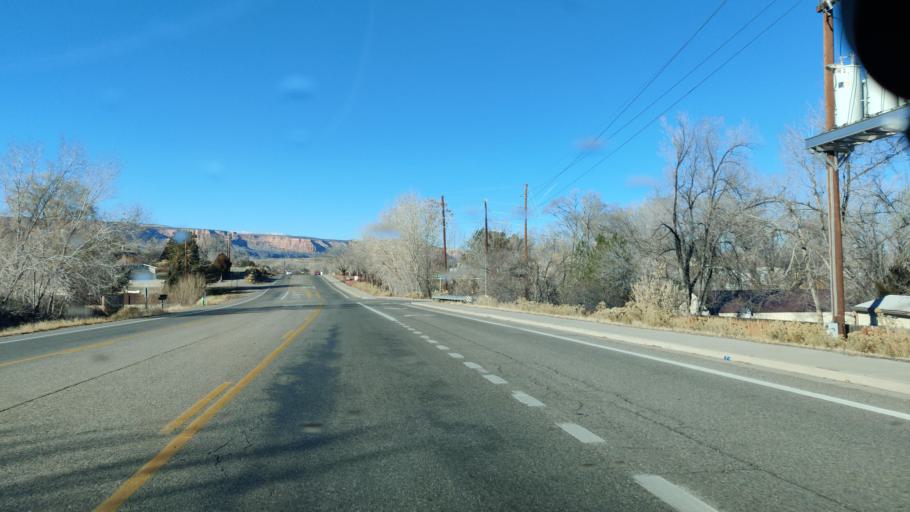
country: US
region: Colorado
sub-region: Mesa County
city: Redlands
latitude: 39.0690
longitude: -108.6109
